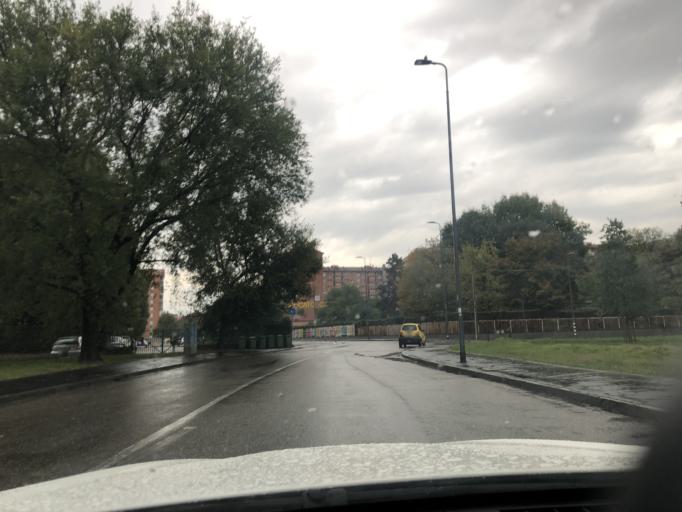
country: IT
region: Lombardy
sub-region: Citta metropolitana di Milano
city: Baranzate
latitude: 45.4898
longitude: 9.1232
